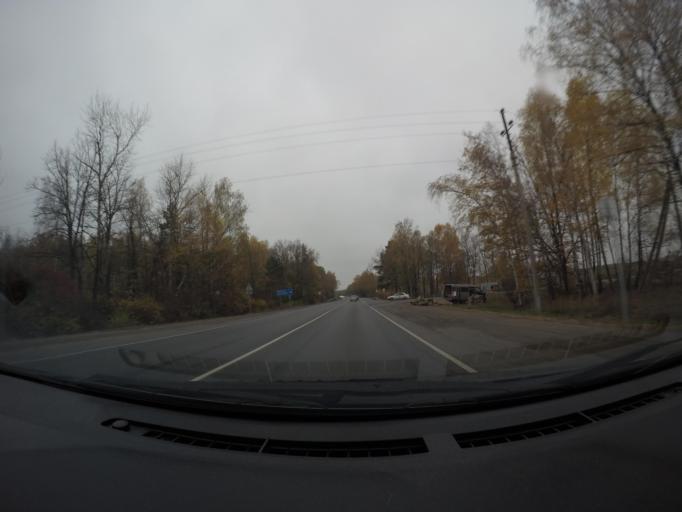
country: RU
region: Moskovskaya
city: Malyshevo
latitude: 55.4581
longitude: 38.3297
